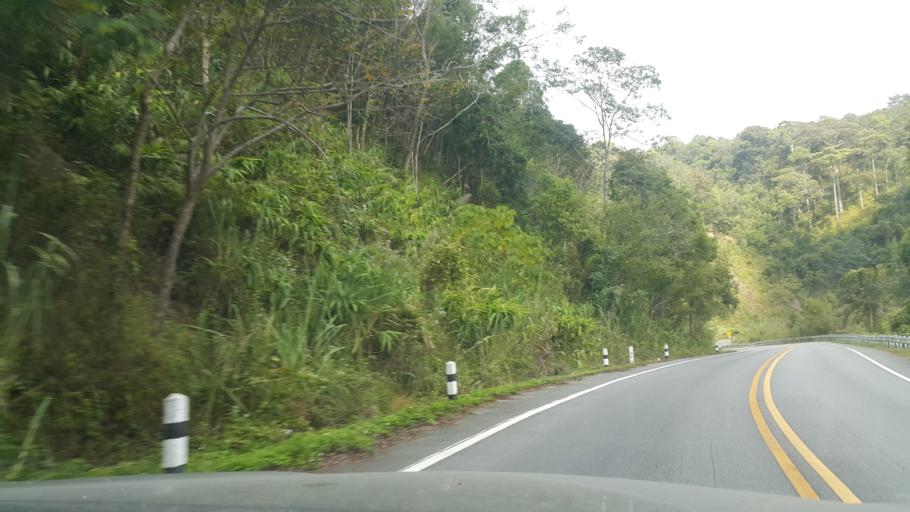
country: TH
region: Phayao
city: Phayao
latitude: 19.0717
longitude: 99.7707
